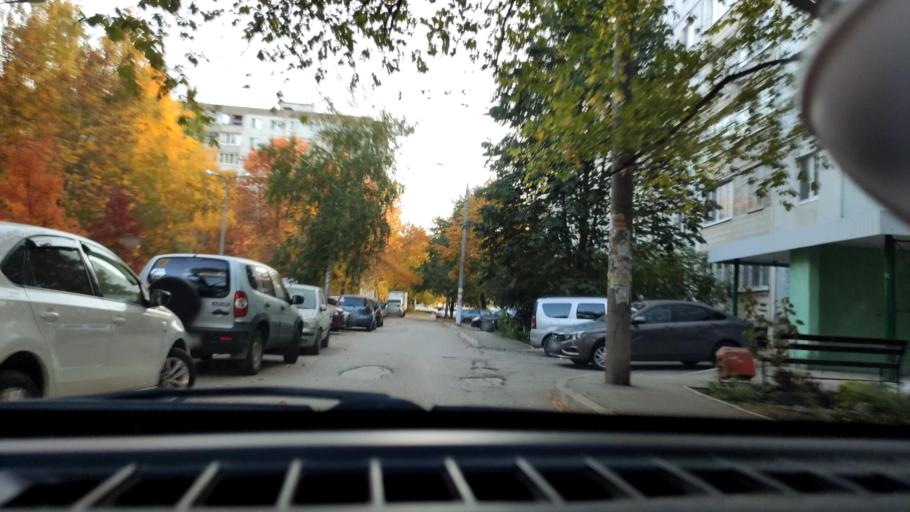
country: RU
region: Samara
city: Samara
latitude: 53.2602
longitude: 50.2352
